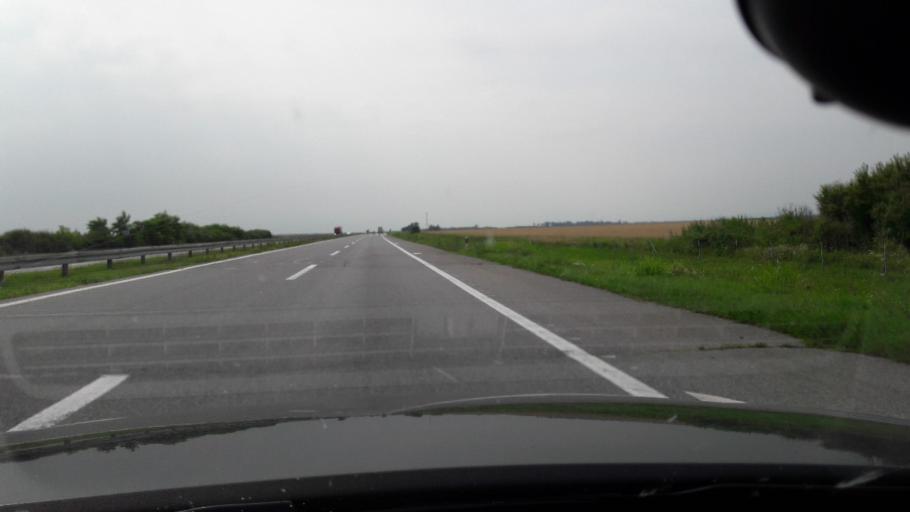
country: RS
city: Budanovci
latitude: 44.9406
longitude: 19.8809
